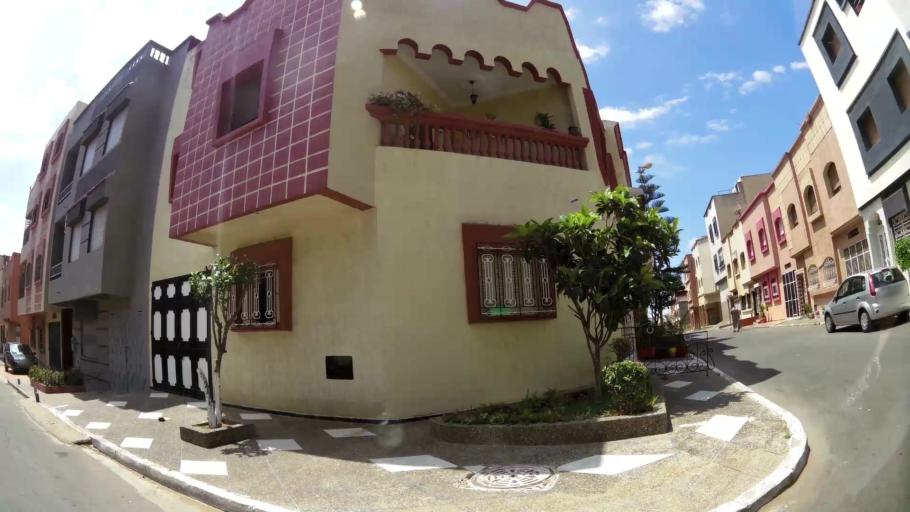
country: MA
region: Gharb-Chrarda-Beni Hssen
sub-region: Kenitra Province
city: Kenitra
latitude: 34.2749
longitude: -6.6058
